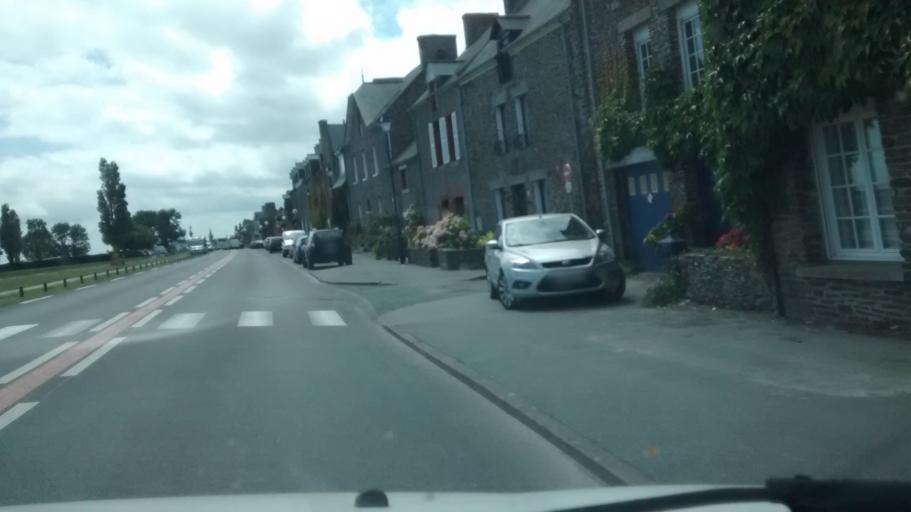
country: FR
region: Brittany
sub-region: Departement d'Ille-et-Vilaine
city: La Fresnais
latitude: 48.6209
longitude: -1.8529
